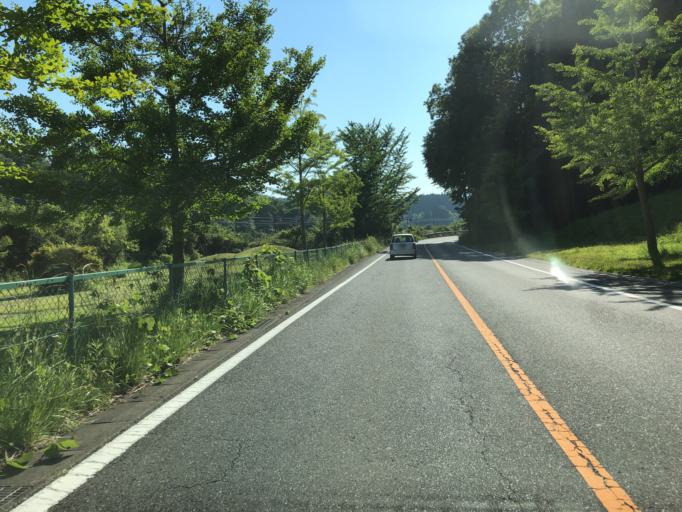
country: JP
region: Fukushima
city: Iwaki
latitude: 36.9403
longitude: 140.8155
